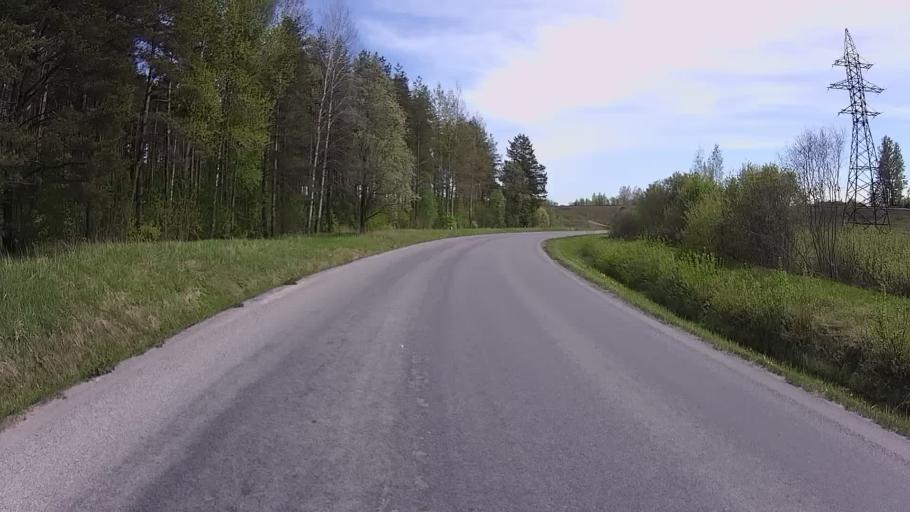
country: EE
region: Valgamaa
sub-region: Valga linn
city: Valga
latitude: 57.7770
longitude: 26.0708
